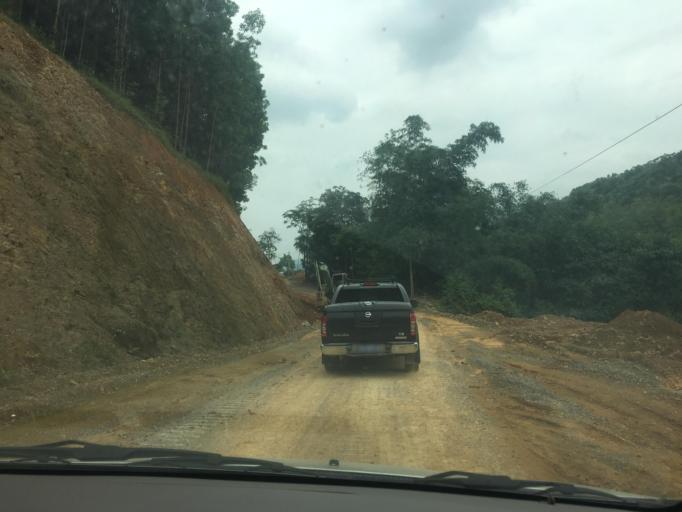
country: VN
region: Lang Son
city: Binh Gia
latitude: 22.1268
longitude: 106.3528
